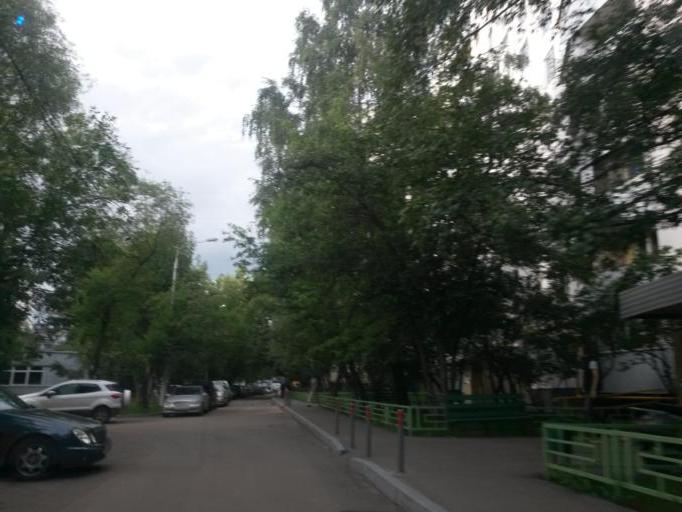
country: RU
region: Moscow
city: Orekhovo-Borisovo
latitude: 55.6082
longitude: 37.7168
